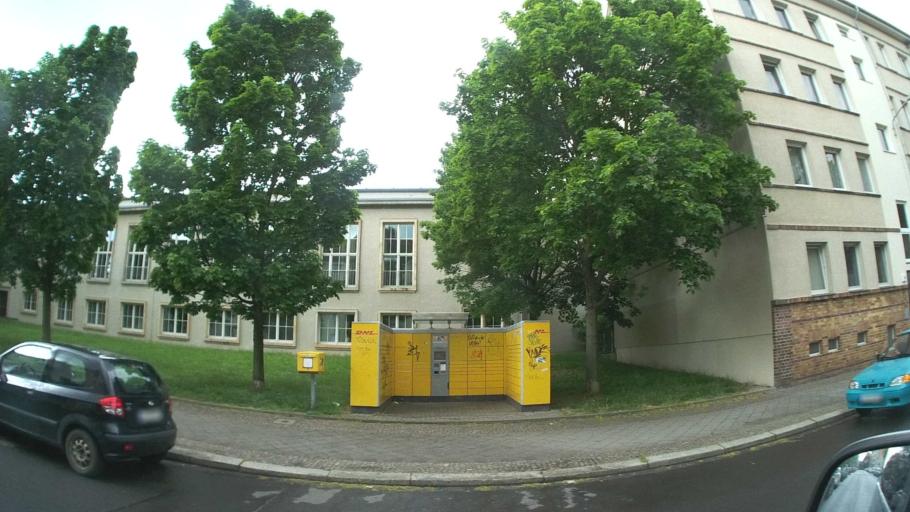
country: DE
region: Saxony
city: Leipzig
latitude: 51.3133
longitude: 12.3765
